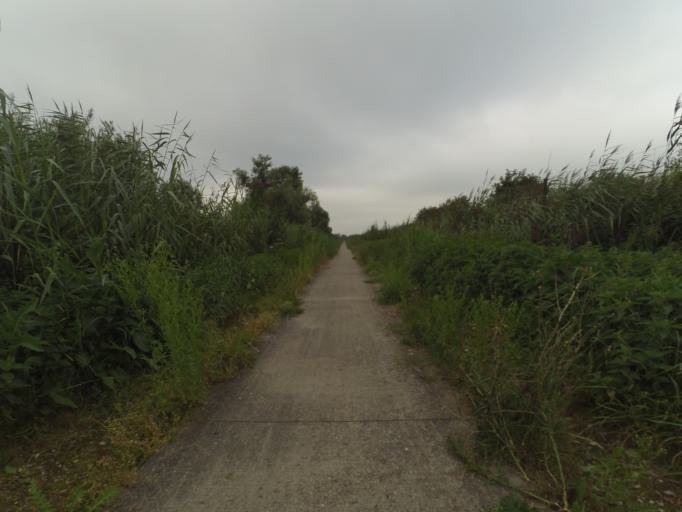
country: NL
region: Flevoland
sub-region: Gemeente Lelystad
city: Lelystad
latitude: 52.4351
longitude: 5.4147
